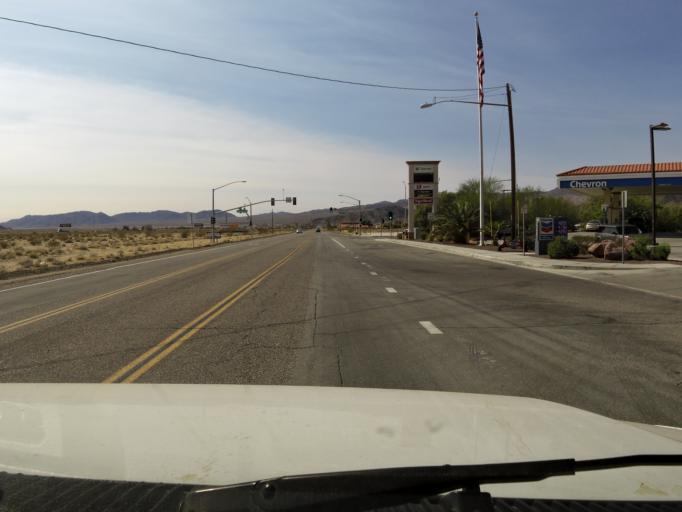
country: US
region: California
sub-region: San Bernardino County
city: Fort Irwin
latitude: 35.2771
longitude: -116.0566
